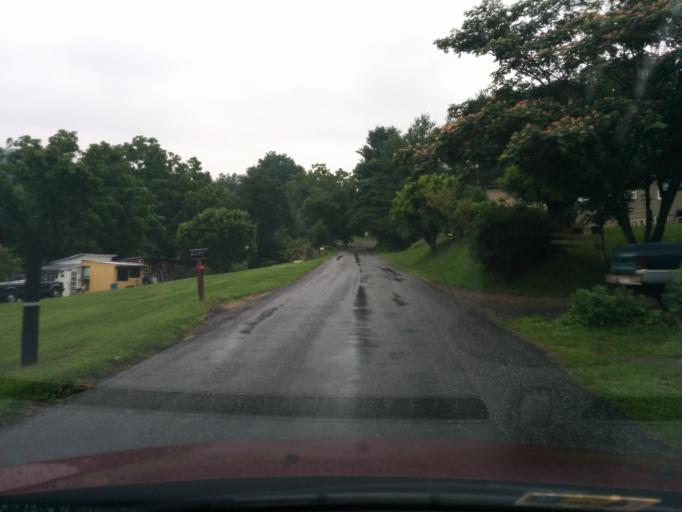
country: US
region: Virginia
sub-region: Rockbridge County
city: East Lexington
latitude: 37.8284
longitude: -79.4397
